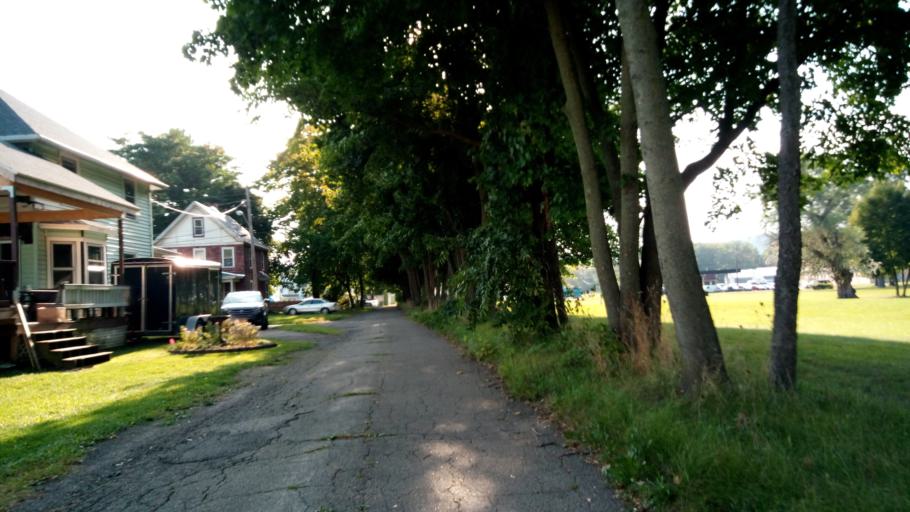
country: US
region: New York
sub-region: Chemung County
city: Elmira Heights
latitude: 42.1150
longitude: -76.8062
